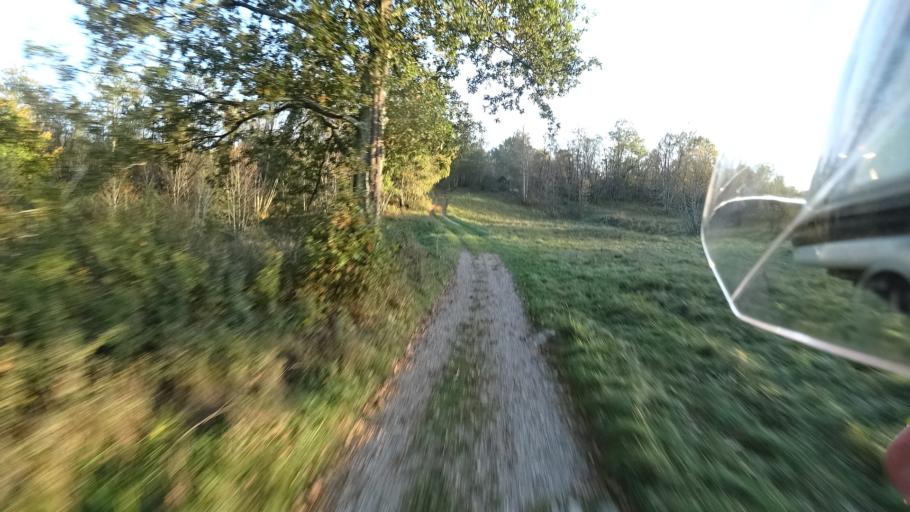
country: HR
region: Primorsko-Goranska
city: Kastav
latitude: 45.4162
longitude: 14.3122
